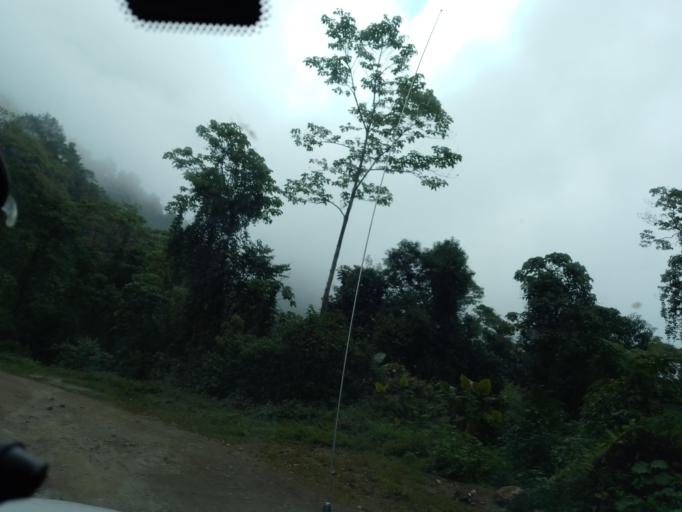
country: MX
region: Chiapas
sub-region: Union Juarez
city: Santo Domingo
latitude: 15.0912
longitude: -92.0973
